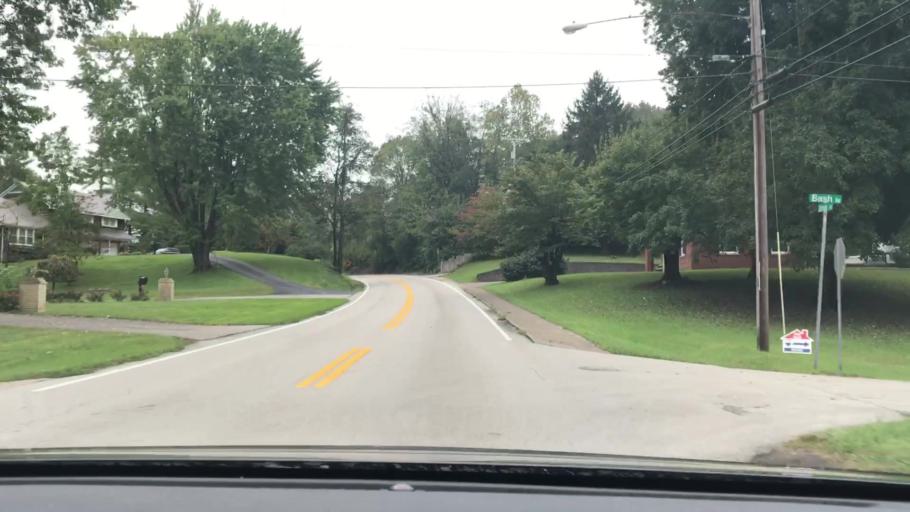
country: US
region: Kentucky
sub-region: Pulaski County
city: Somerset
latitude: 37.0914
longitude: -84.5925
